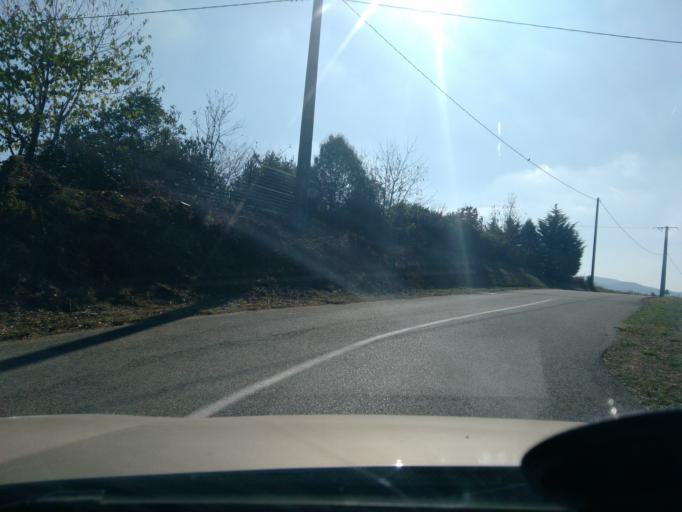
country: FR
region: Rhone-Alpes
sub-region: Departement de la Drome
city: Montboucher-sur-Jabron
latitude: 44.5530
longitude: 4.8128
